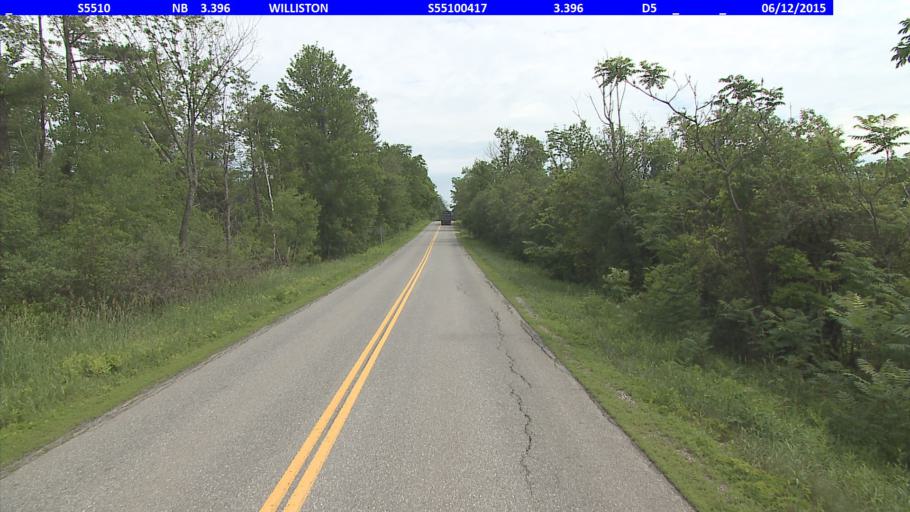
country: US
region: Vermont
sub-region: Chittenden County
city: Williston
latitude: 44.4191
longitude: -73.0823
